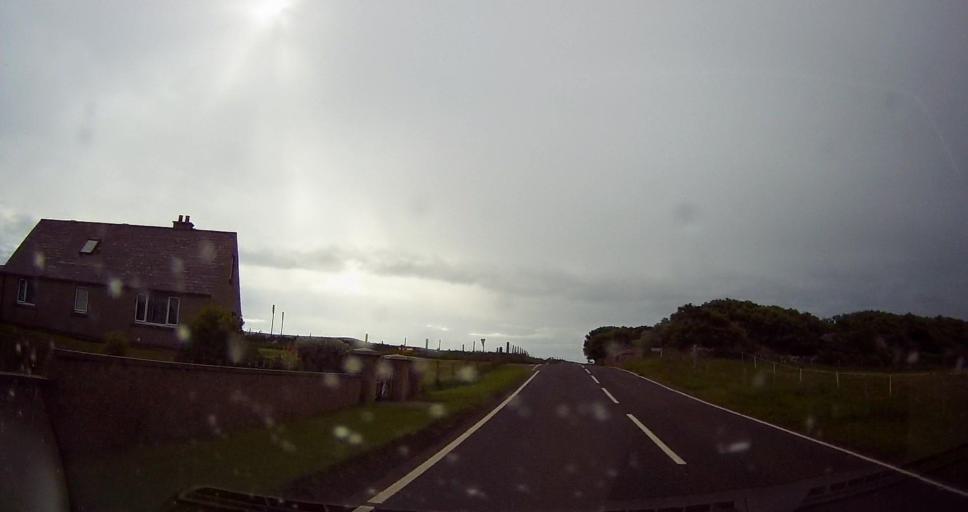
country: GB
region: Scotland
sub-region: Orkney Islands
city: Stromness
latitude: 59.0480
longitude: -3.1978
